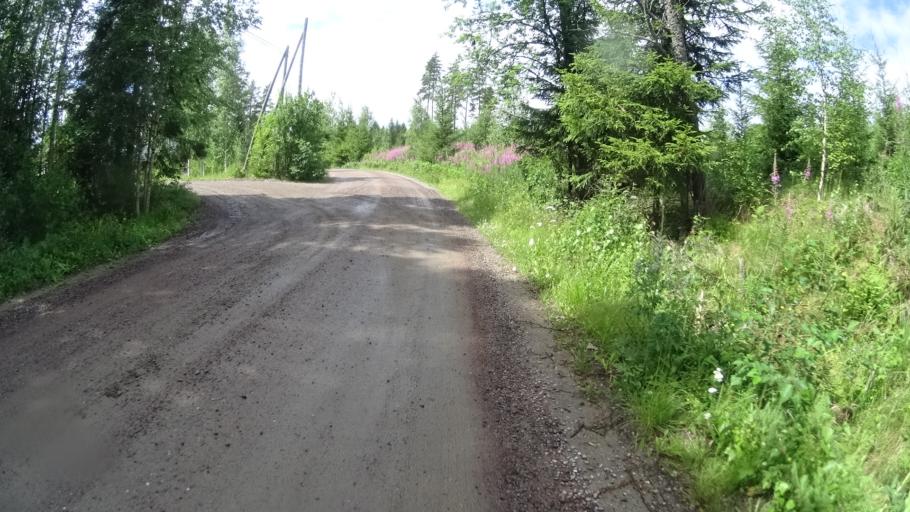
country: FI
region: Uusimaa
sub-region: Helsinki
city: Karkkila
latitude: 60.5859
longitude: 24.3190
